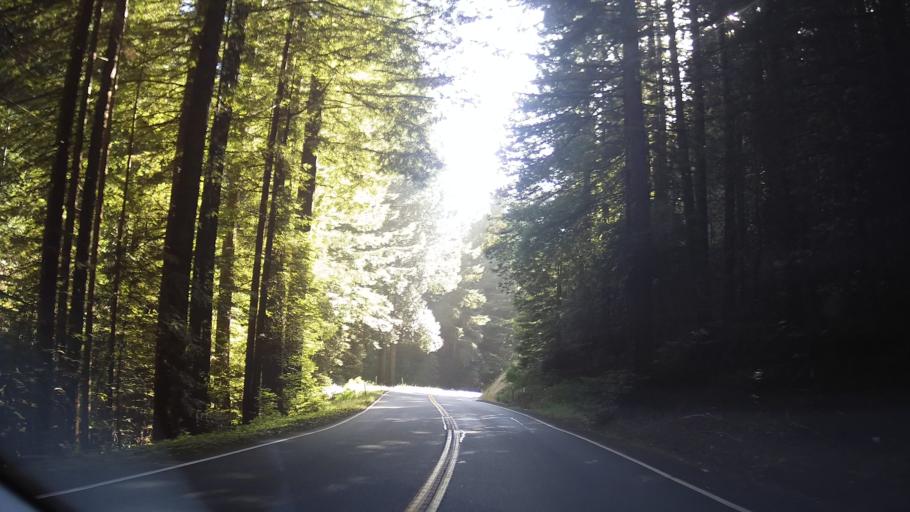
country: US
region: California
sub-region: Mendocino County
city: Brooktrails
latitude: 39.3488
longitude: -123.5826
